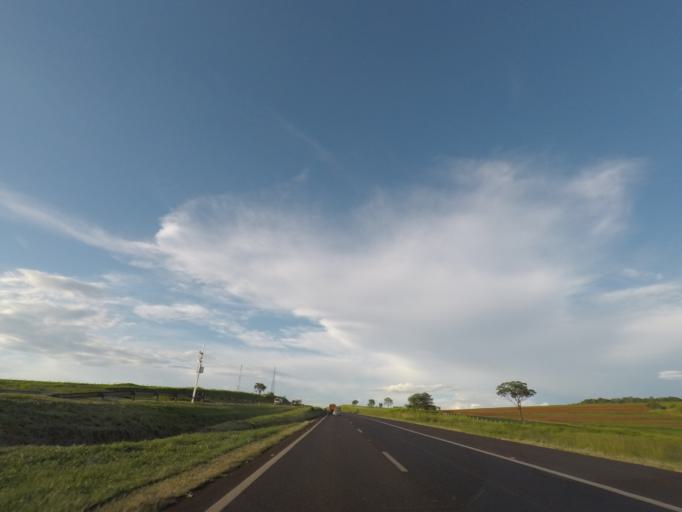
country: BR
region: Sao Paulo
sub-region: Ituverava
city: Ituverava
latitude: -20.2769
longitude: -47.7974
